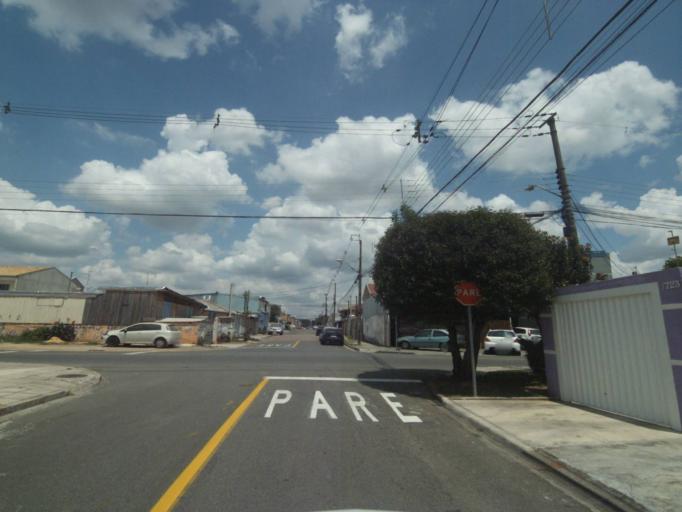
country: BR
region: Parana
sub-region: Sao Jose Dos Pinhais
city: Sao Jose dos Pinhais
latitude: -25.5369
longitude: -49.2619
